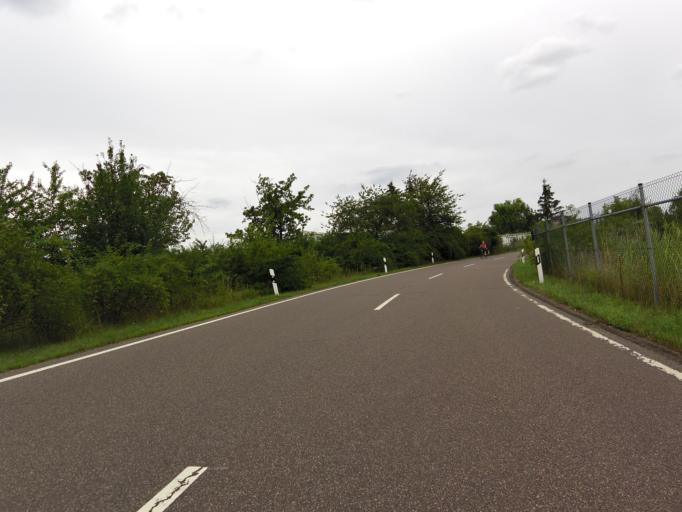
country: DE
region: Saxony
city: Rackwitz
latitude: 51.4198
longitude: 12.3803
